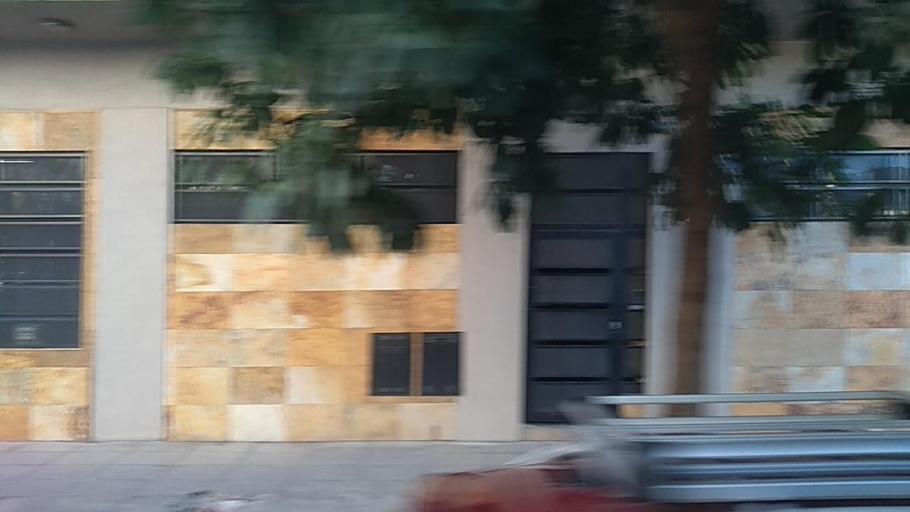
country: AR
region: Buenos Aires F.D.
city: Villa Santa Rita
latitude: -34.6190
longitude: -58.5127
